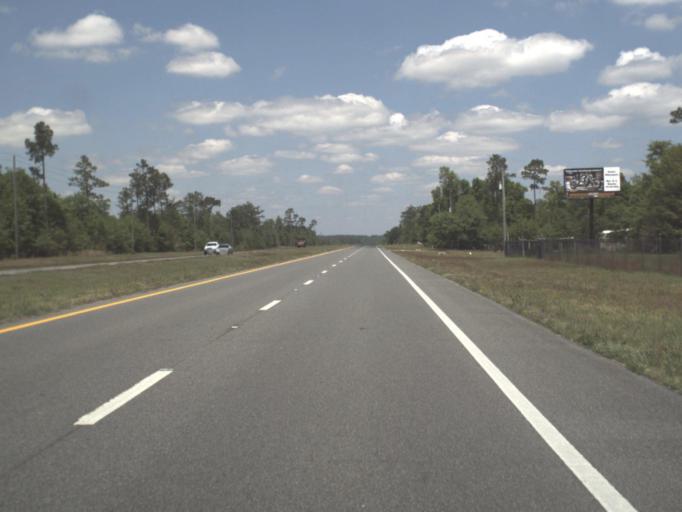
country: US
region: Florida
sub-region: Santa Rosa County
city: Point Baker
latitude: 30.6962
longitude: -87.0523
